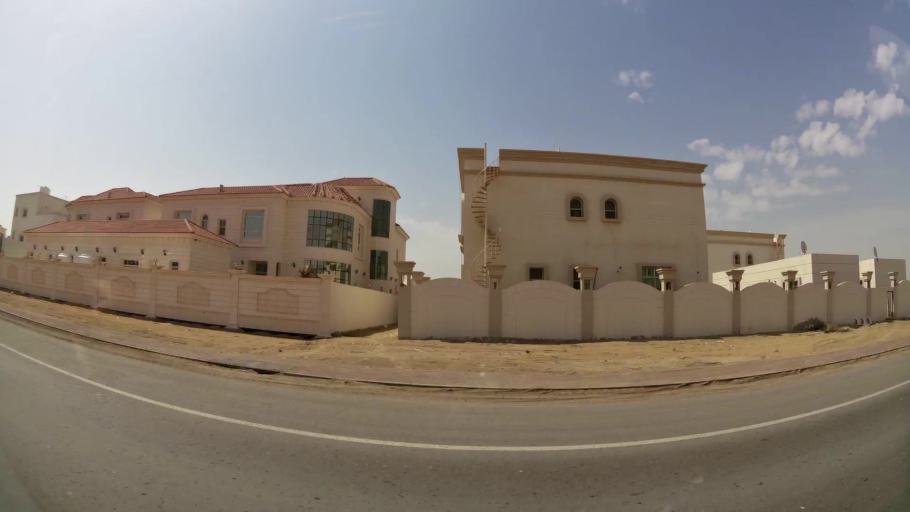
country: AE
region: Abu Dhabi
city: Abu Dhabi
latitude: 24.3123
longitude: 54.5748
